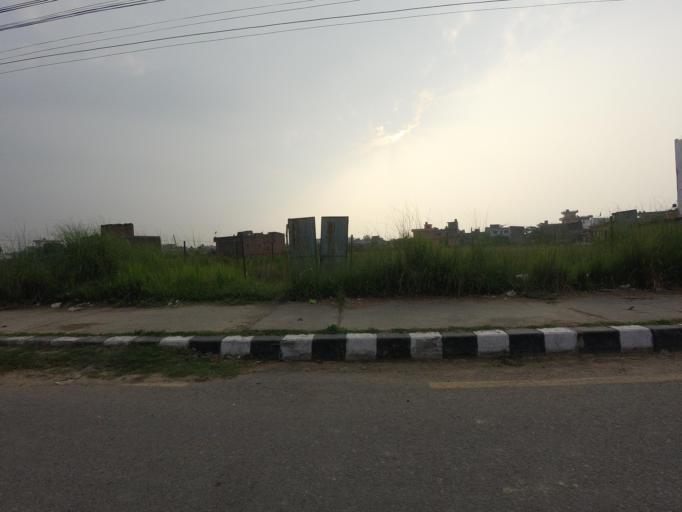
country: NP
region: Western Region
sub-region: Lumbini Zone
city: Bhairahawa
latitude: 27.5028
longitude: 83.4439
